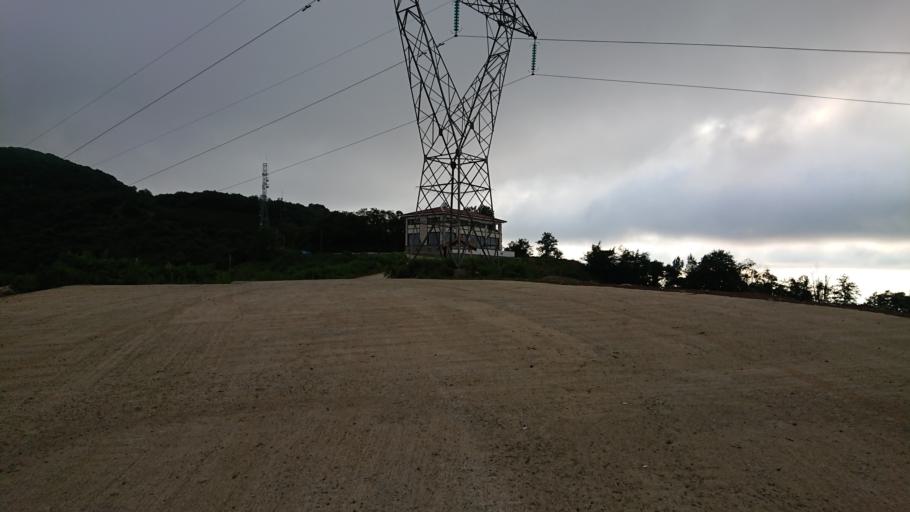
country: TR
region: Rize
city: Rize
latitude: 40.9911
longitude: 40.5119
